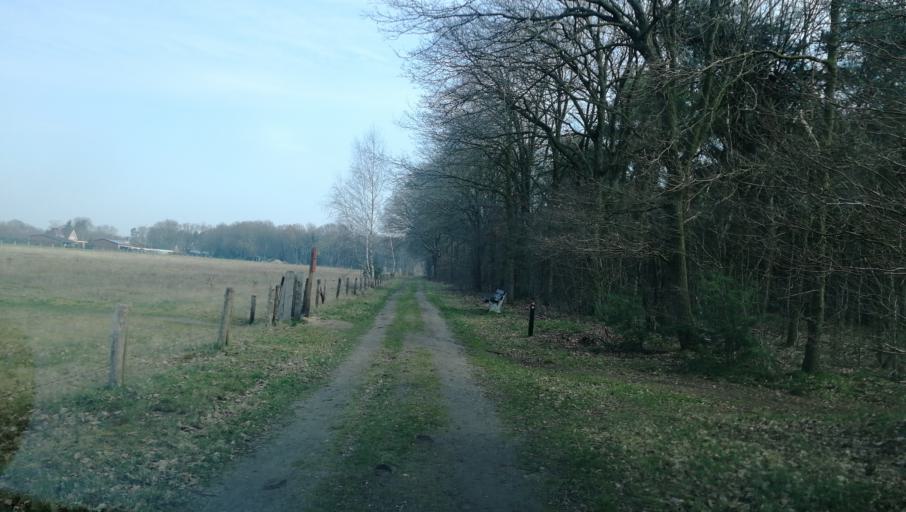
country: NL
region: Limburg
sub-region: Gemeente Peel en Maas
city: Maasbree
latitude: 51.4343
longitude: 6.0638
